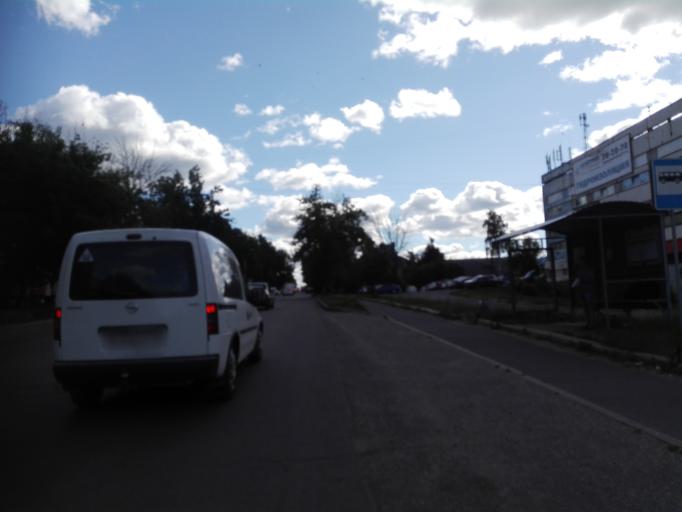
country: RU
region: Orjol
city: Orel
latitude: 52.9512
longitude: 36.0417
